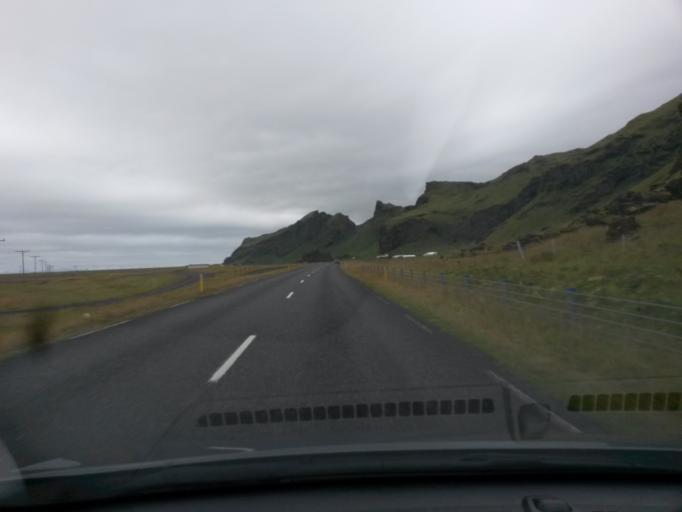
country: IS
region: South
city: Vestmannaeyjar
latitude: 63.5220
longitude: -19.5286
